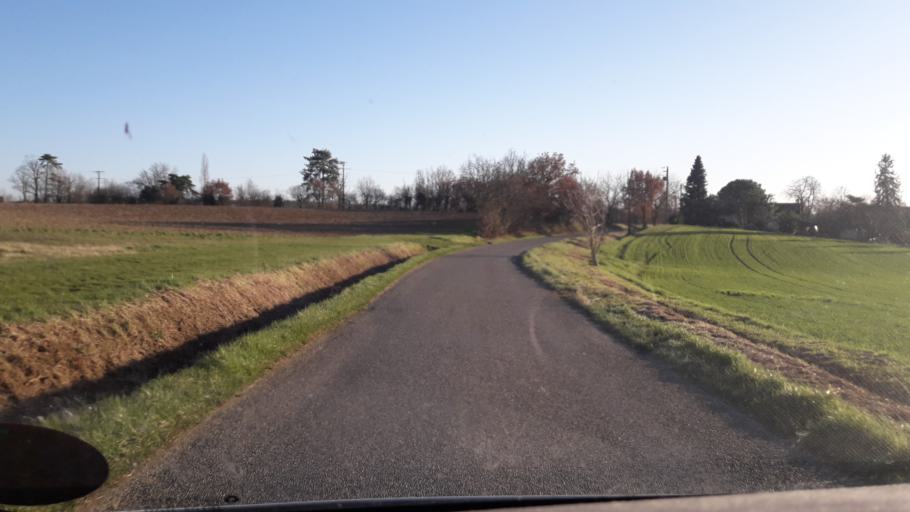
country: FR
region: Midi-Pyrenees
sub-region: Departement du Gers
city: Gimont
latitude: 43.6202
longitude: 0.9743
